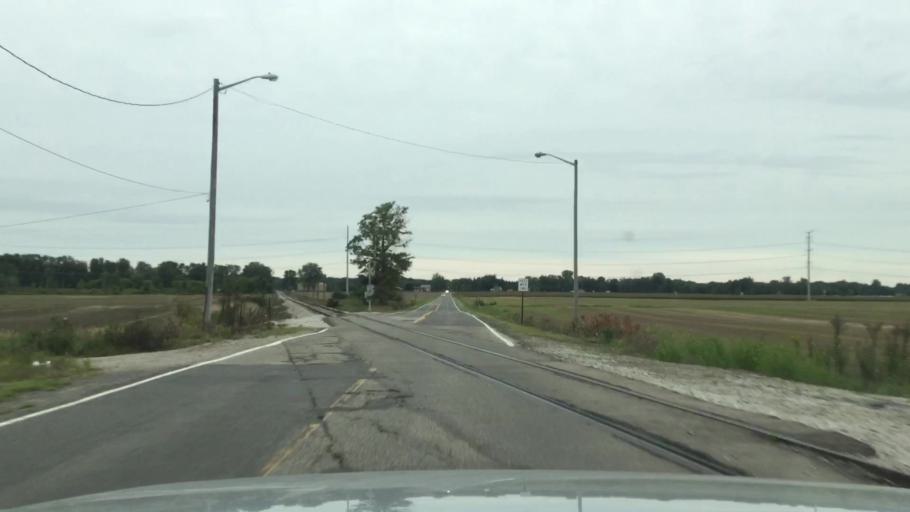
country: US
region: Michigan
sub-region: Washtenaw County
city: Milan
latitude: 42.1151
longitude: -83.6961
